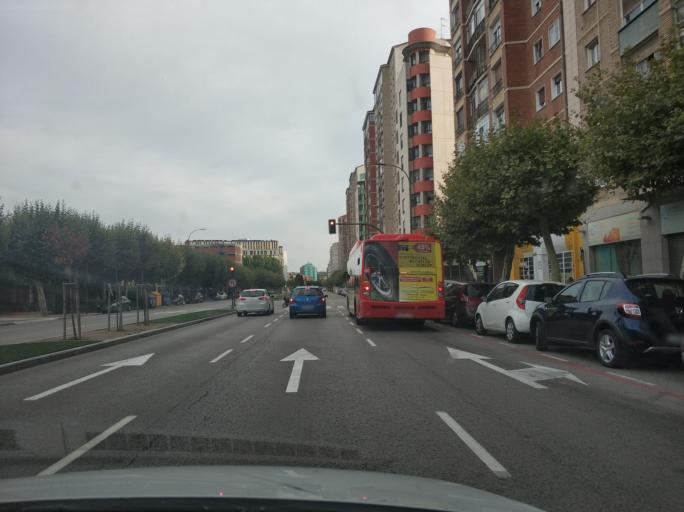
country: ES
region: Castille and Leon
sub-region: Provincia de Burgos
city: Burgos
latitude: 42.3530
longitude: -3.6909
